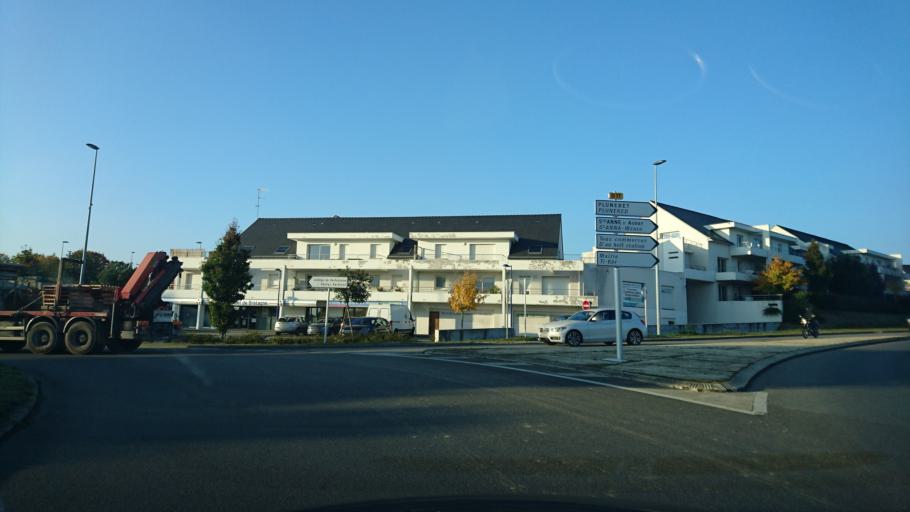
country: FR
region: Brittany
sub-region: Departement du Morbihan
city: Pluneret
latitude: 47.6716
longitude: -2.9616
